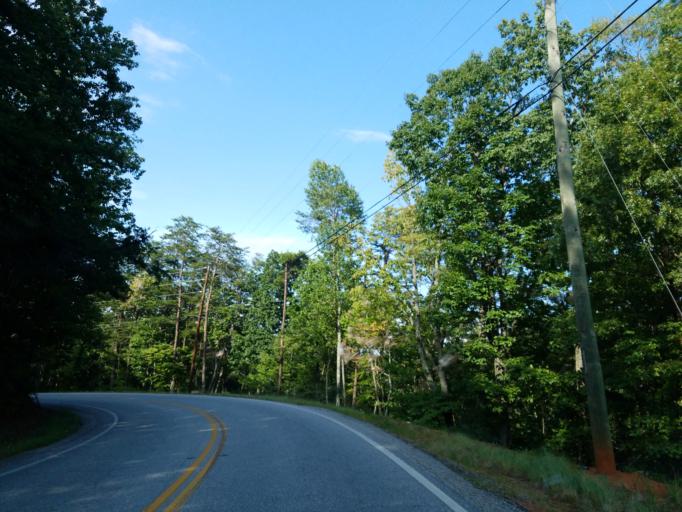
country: US
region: Georgia
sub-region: Lumpkin County
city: Dahlonega
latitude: 34.6044
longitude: -83.9690
